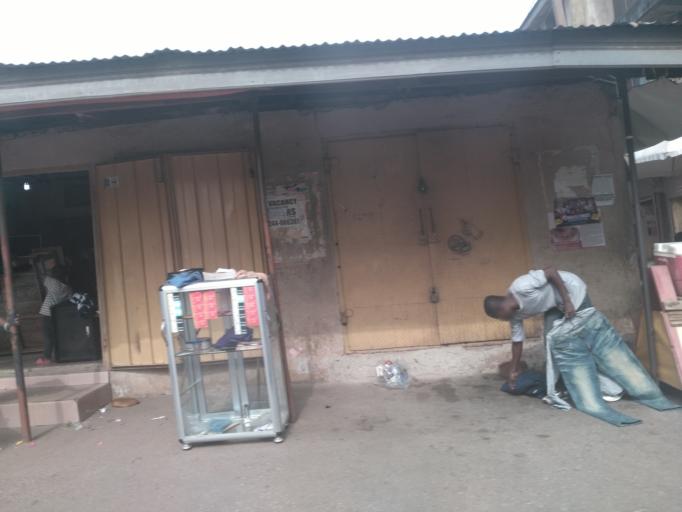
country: GH
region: Ashanti
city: Kumasi
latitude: 6.7015
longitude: -1.6199
